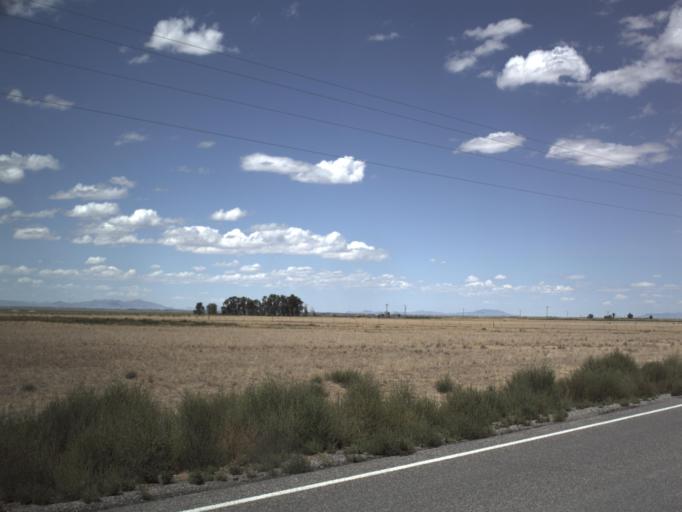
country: US
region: Utah
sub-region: Millard County
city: Delta
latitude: 39.1922
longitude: -112.4100
